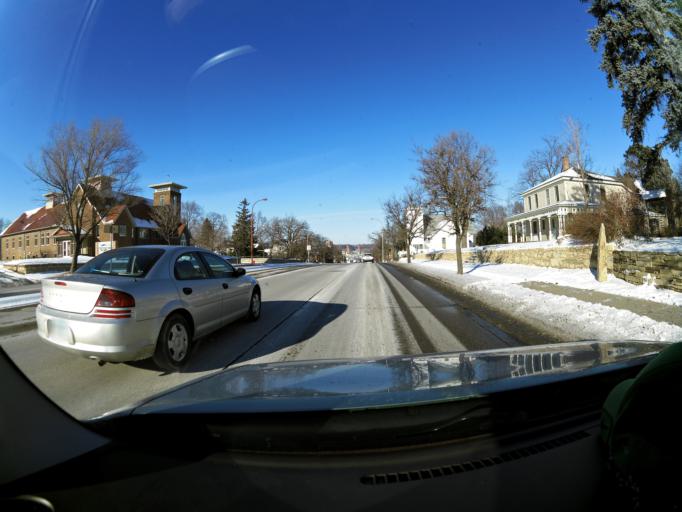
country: US
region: Minnesota
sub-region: Dakota County
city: Hastings
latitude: 44.7376
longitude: -92.8525
